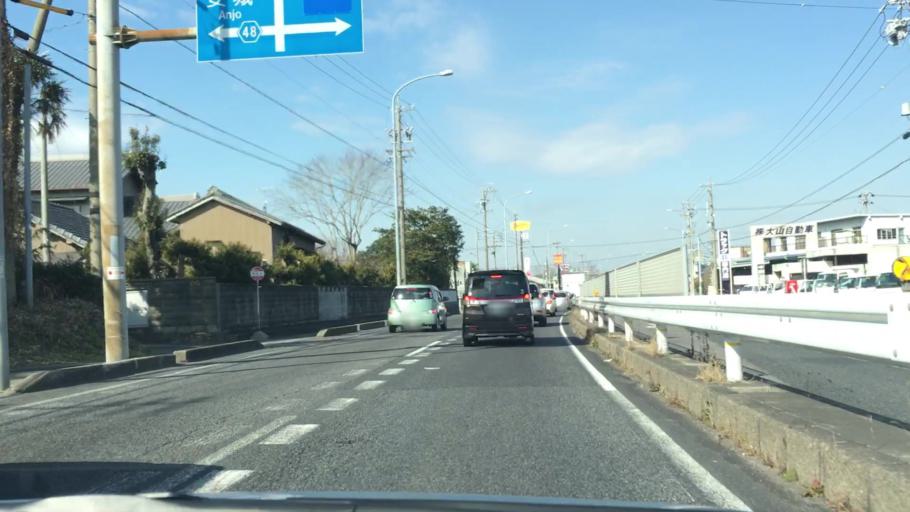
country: JP
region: Aichi
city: Okazaki
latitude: 34.9291
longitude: 137.1982
